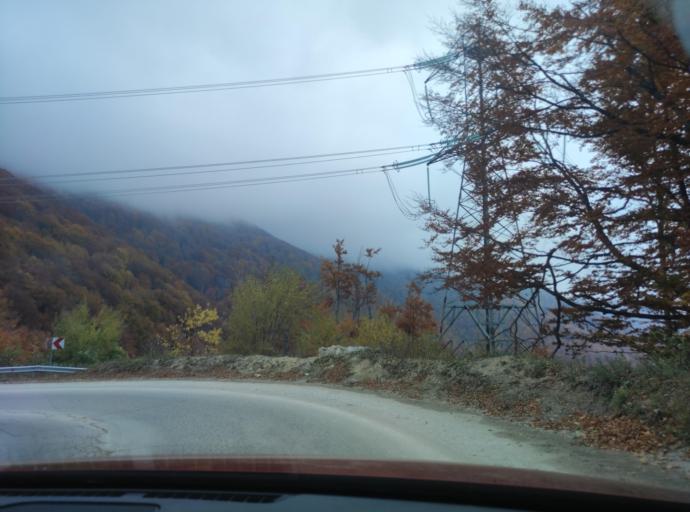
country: BG
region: Montana
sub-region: Obshtina Berkovitsa
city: Berkovitsa
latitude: 43.1292
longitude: 23.1354
